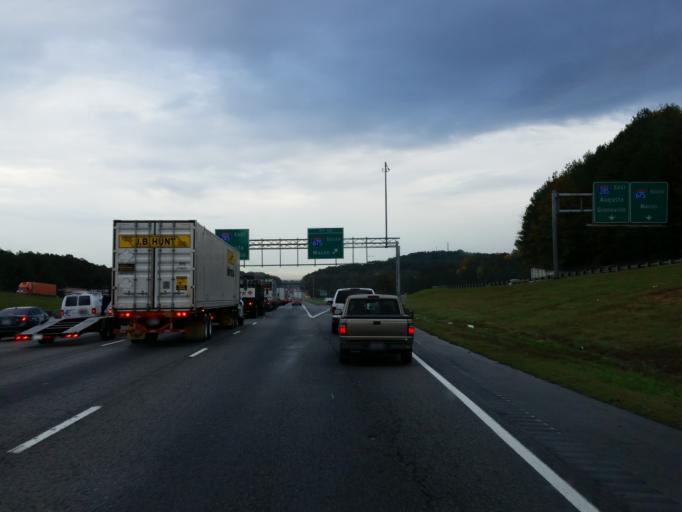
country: US
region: Georgia
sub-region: Clayton County
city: Conley
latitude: 33.6679
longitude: -84.3399
